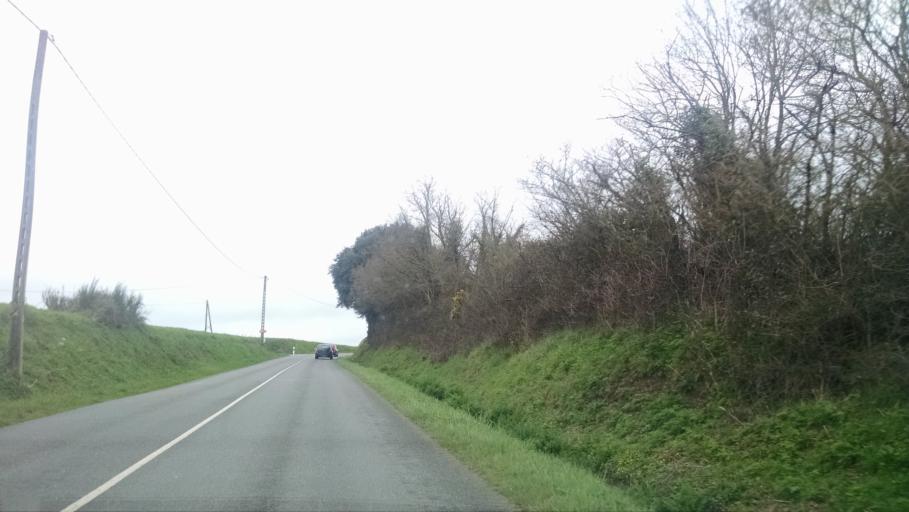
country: FR
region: Pays de la Loire
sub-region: Departement de la Loire-Atlantique
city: Monnieres
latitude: 47.1413
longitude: -1.3548
